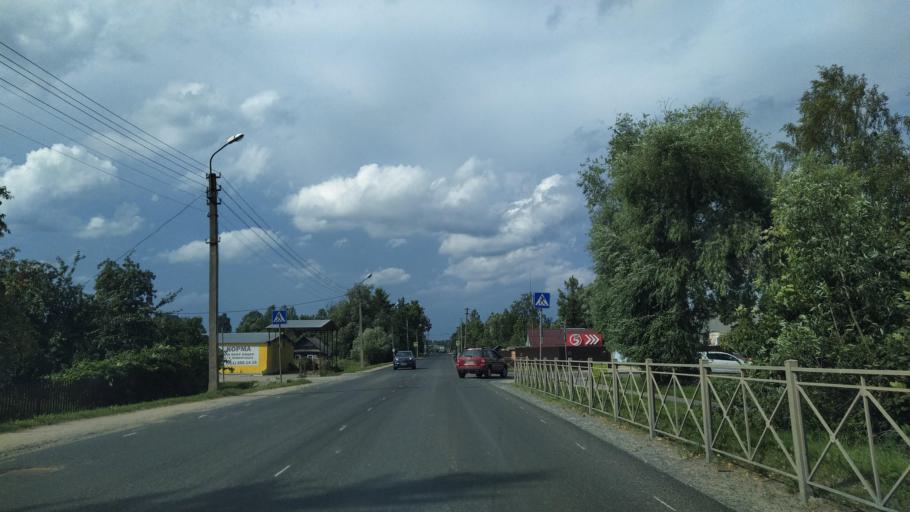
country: RU
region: Pskov
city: Porkhov
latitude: 57.7641
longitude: 29.5552
